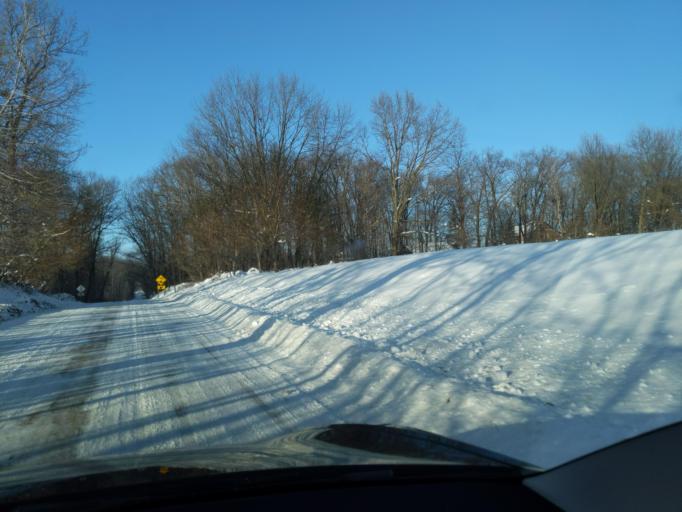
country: US
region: Michigan
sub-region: Ingham County
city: Stockbridge
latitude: 42.4600
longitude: -84.1187
